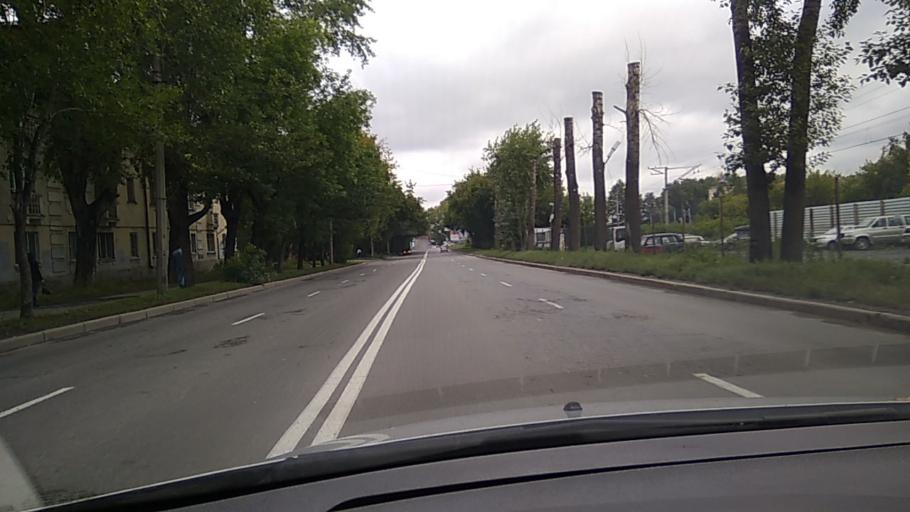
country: RU
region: Sverdlovsk
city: Sovkhoznyy
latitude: 56.7658
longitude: 60.6138
